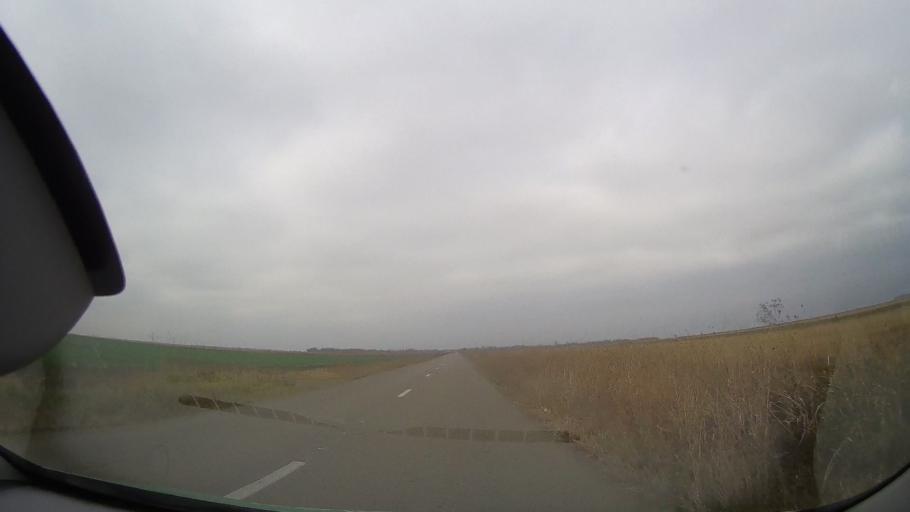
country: RO
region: Buzau
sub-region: Comuna Scutelnici
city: Scutelnici
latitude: 44.8640
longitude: 26.8965
